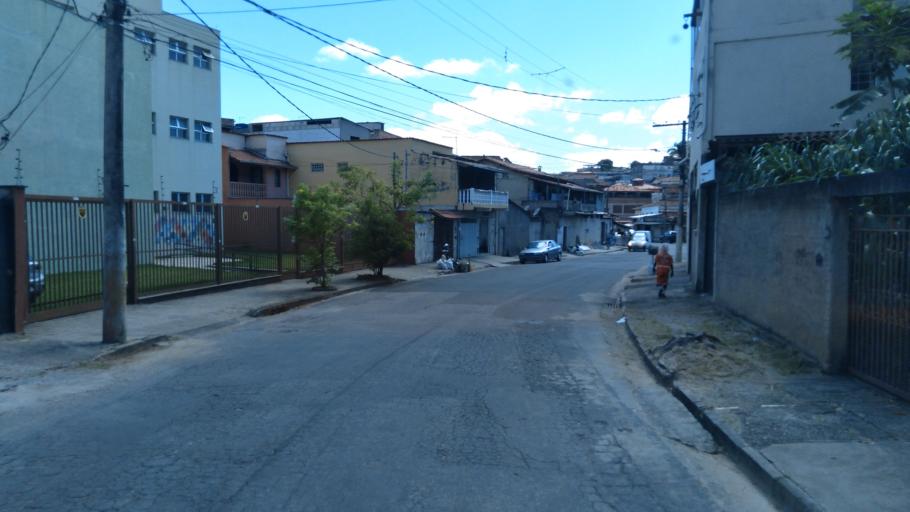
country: BR
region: Minas Gerais
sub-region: Belo Horizonte
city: Belo Horizonte
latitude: -19.8613
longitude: -43.9072
